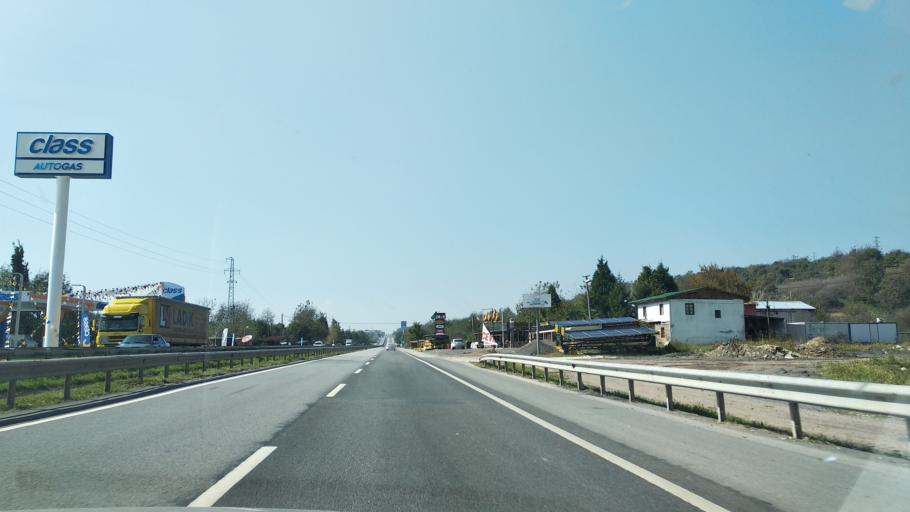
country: TR
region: Kocaeli
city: Derbent
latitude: 40.7324
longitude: 30.1926
